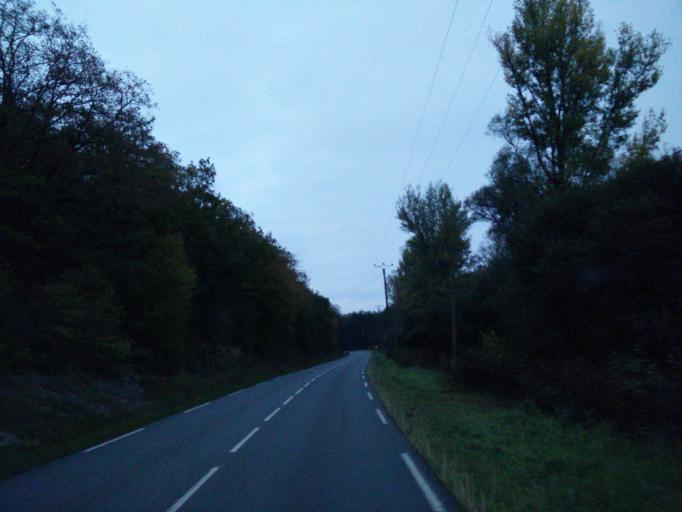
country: FR
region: Aquitaine
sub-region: Departement de la Dordogne
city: Saint-Cyprien
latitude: 44.9233
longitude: 1.0876
